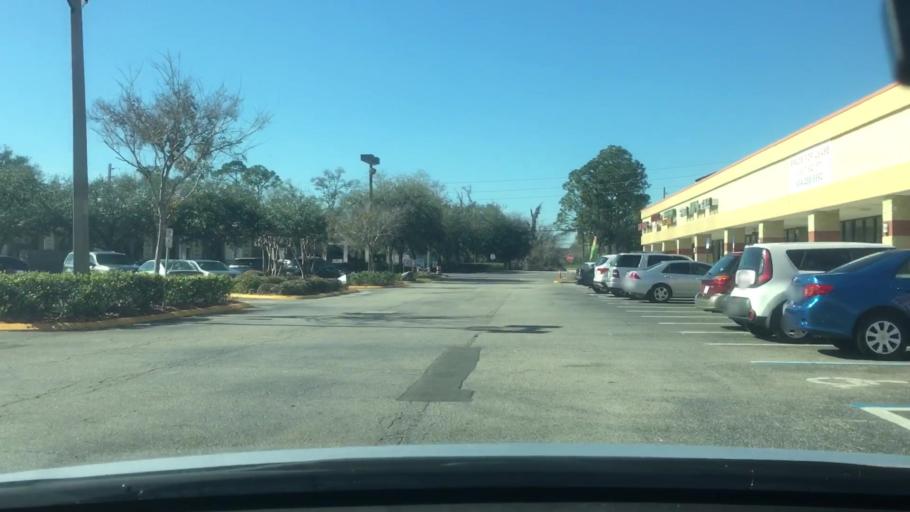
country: US
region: Florida
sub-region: Duval County
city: Atlantic Beach
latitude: 30.3202
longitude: -81.4717
